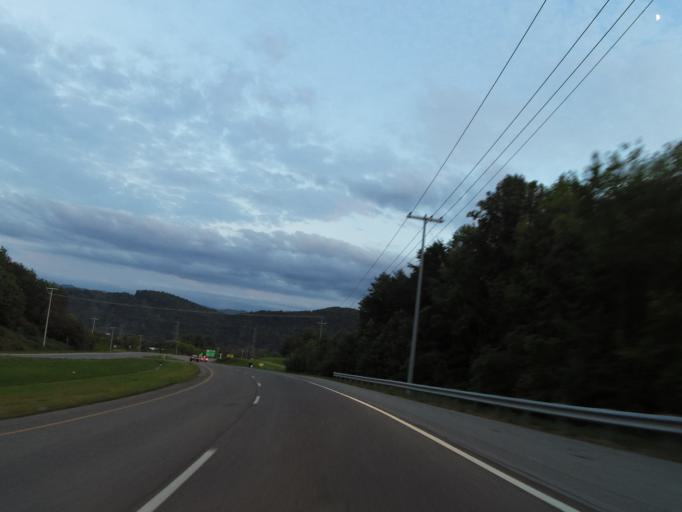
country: US
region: Tennessee
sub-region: Carter County
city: Elizabethton
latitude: 36.3636
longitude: -82.2073
